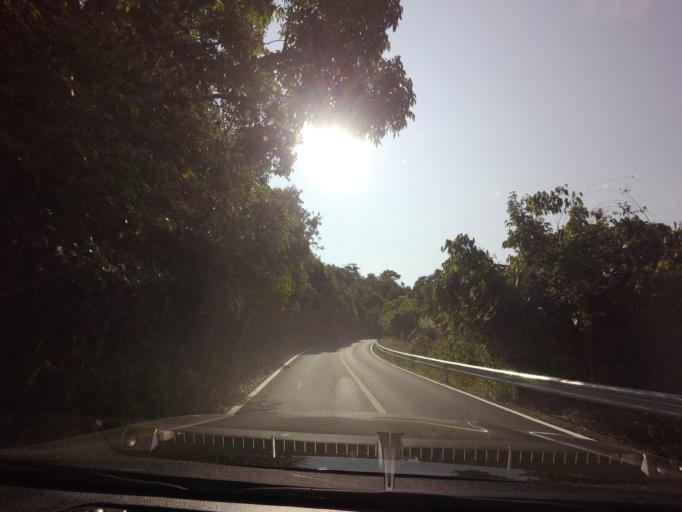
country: TH
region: Kanchanaburi
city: Thong Pha Phum
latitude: 14.6865
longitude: 98.4154
